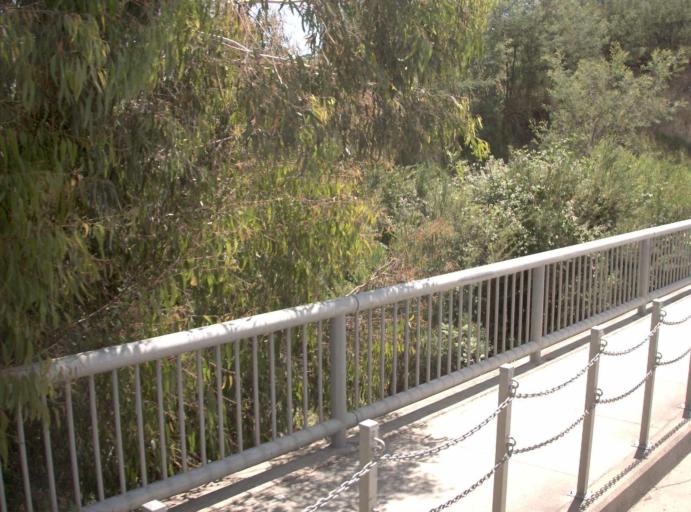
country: AU
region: Victoria
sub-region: East Gippsland
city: Lakes Entrance
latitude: -37.7104
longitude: 147.8359
